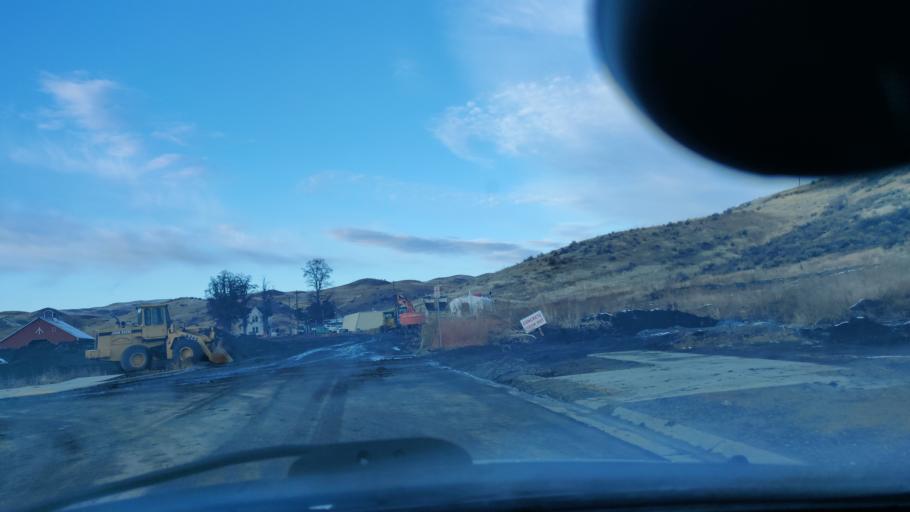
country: US
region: Idaho
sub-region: Ada County
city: Eagle
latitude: 43.7918
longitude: -116.2596
